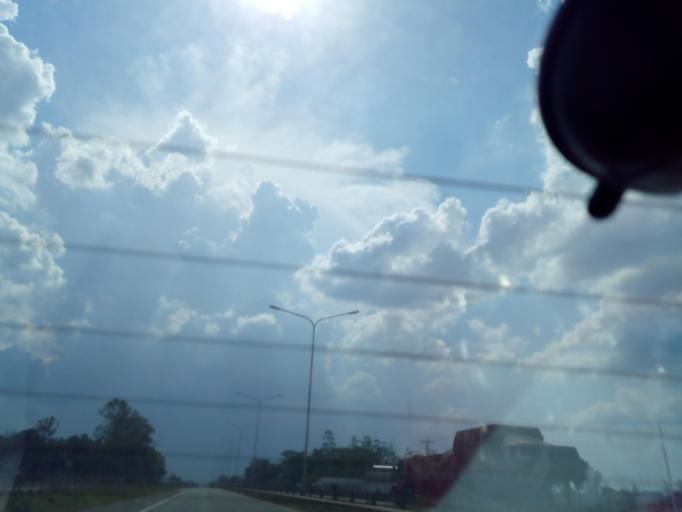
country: AR
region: Corrientes
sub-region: Departamento de Paso de los Libres
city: Paso de los Libres
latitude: -29.7220
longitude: -57.1407
